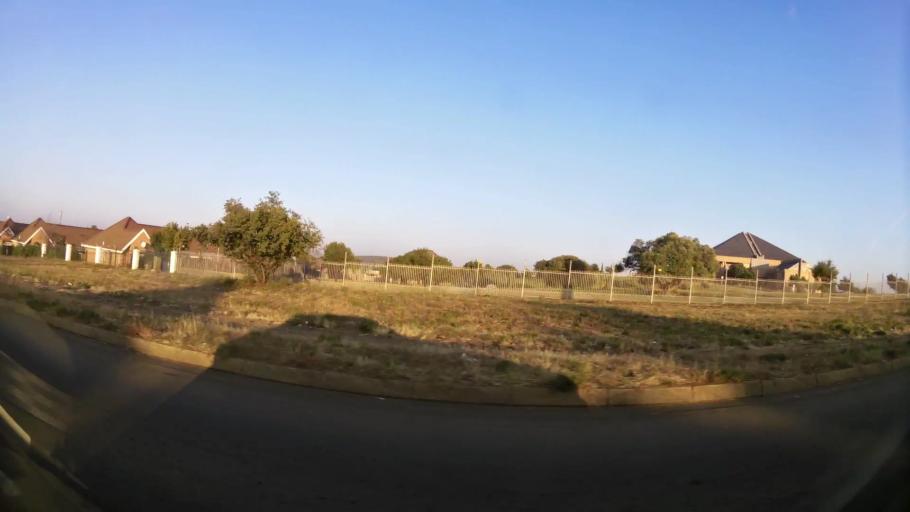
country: ZA
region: Orange Free State
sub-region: Mangaung Metropolitan Municipality
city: Bloemfontein
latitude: -29.0911
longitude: 26.1644
